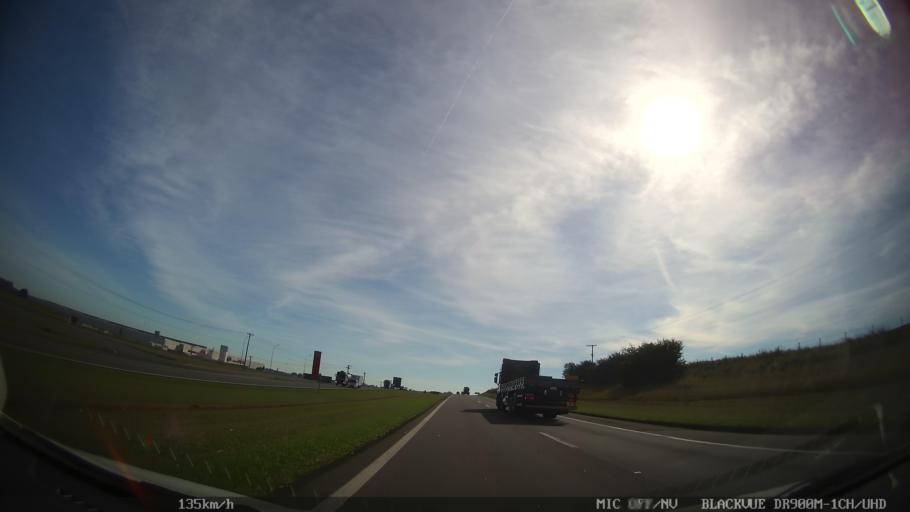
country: BR
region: Sao Paulo
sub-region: Cordeiropolis
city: Cordeiropolis
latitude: -22.4946
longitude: -47.3992
